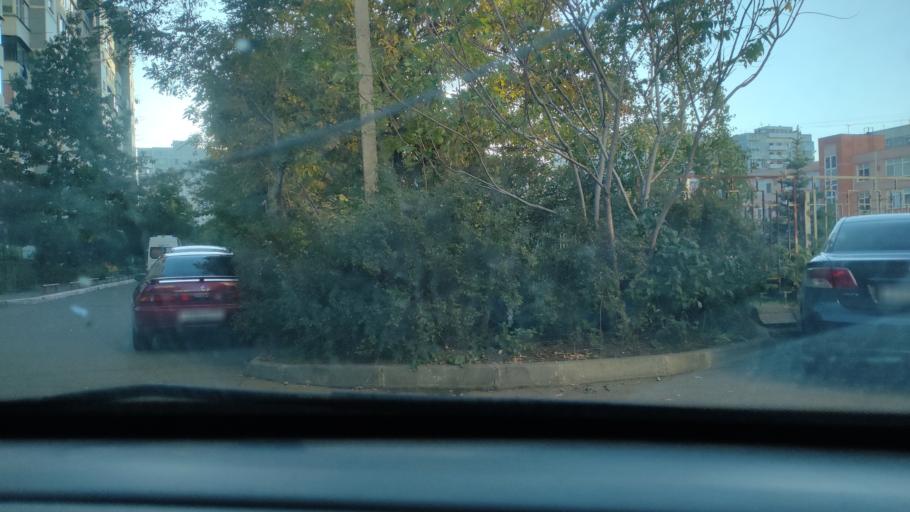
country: RU
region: Adygeya
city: Yablonovskiy
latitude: 45.0279
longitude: 38.9120
